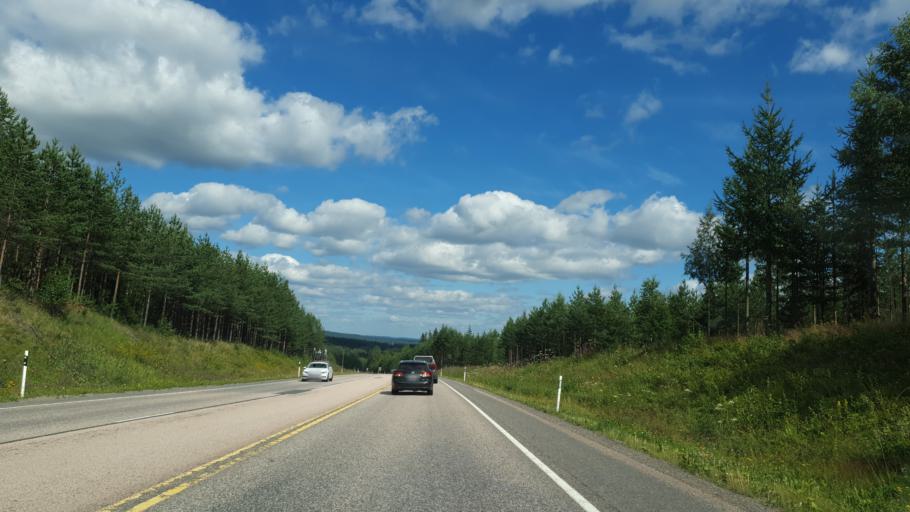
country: FI
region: Central Finland
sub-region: Jaemsae
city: Jaemsae
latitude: 61.8274
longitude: 25.0793
